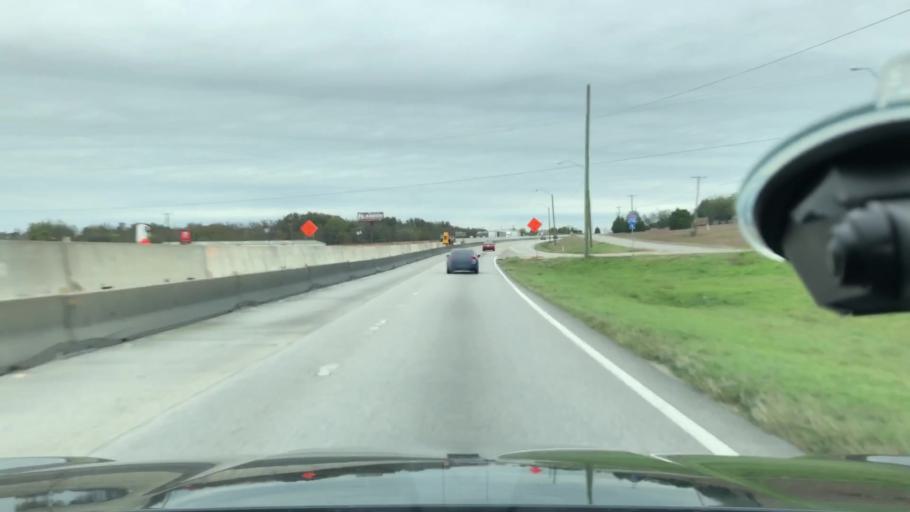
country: US
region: Texas
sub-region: Ellis County
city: Waxahachie
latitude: 32.4114
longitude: -96.8723
